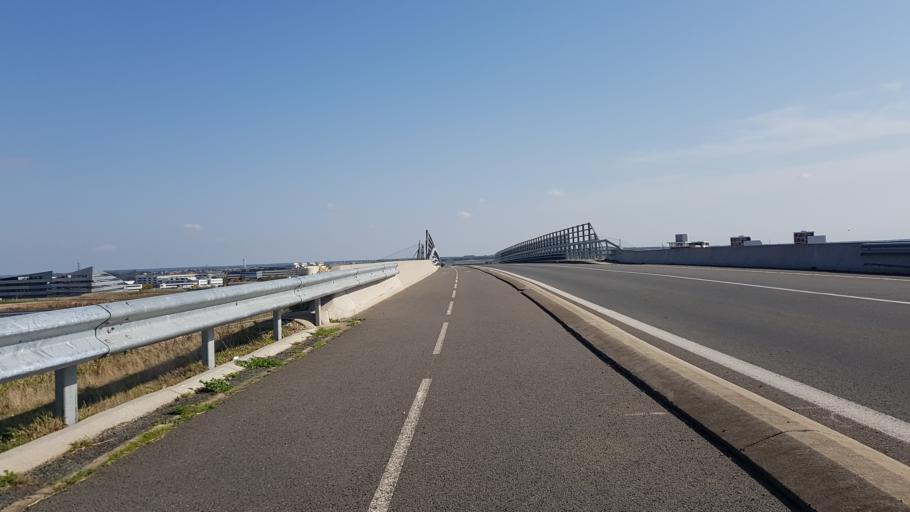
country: FR
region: Poitou-Charentes
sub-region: Departement de la Vienne
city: Chasseneuil-du-Poitou
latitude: 46.6568
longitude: 0.3519
